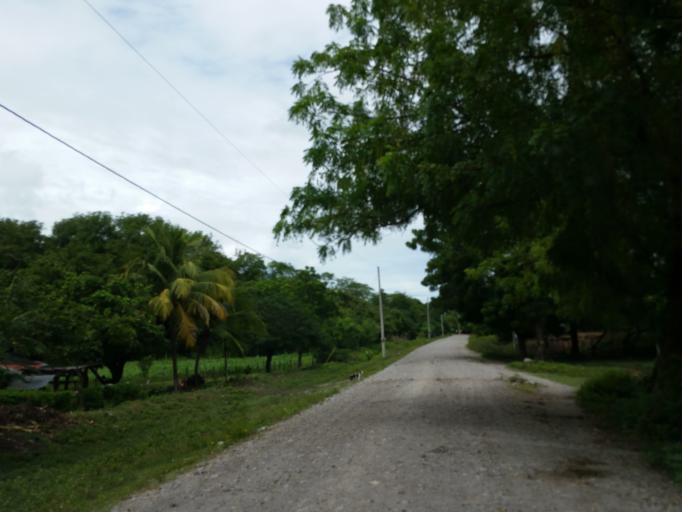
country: NI
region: Leon
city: Telica
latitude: 12.6972
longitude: -86.8662
